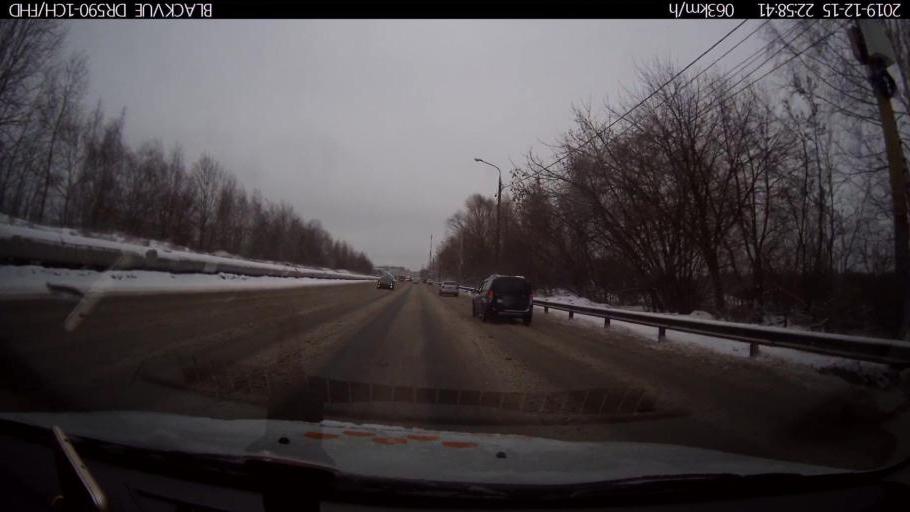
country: RU
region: Nizjnij Novgorod
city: Nizhniy Novgorod
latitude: 56.3428
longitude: 43.9000
